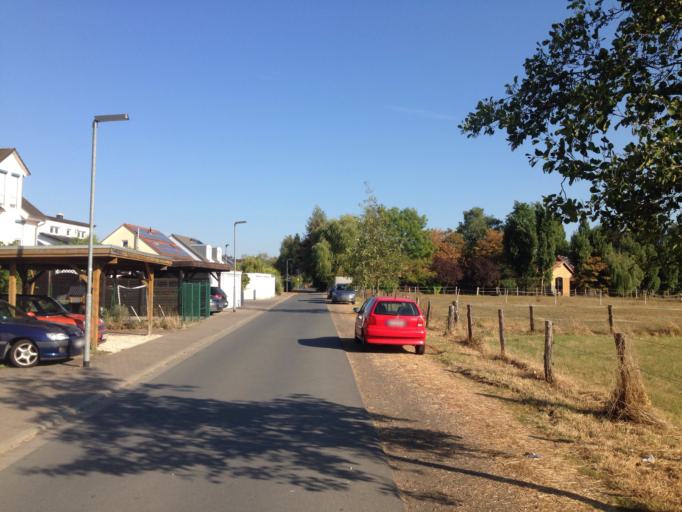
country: DE
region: Hesse
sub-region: Regierungsbezirk Giessen
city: Giessen
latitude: 50.5425
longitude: 8.7299
